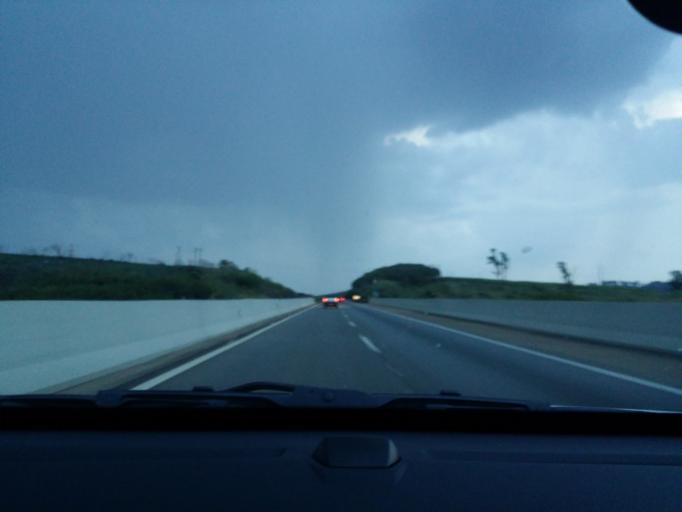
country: BR
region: Sao Paulo
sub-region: Cordeiropolis
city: Cordeiropolis
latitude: -22.5263
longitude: -47.4384
